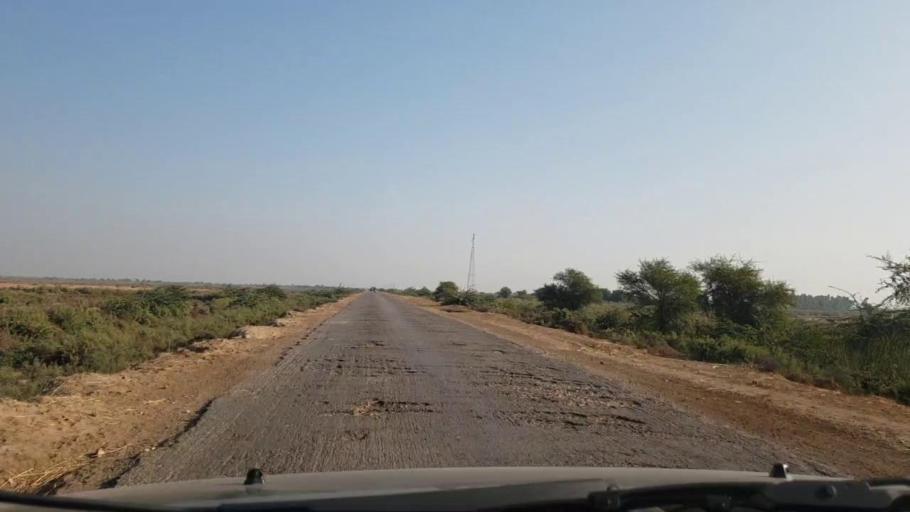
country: PK
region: Sindh
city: Tando Bago
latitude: 24.8389
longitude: 69.0248
